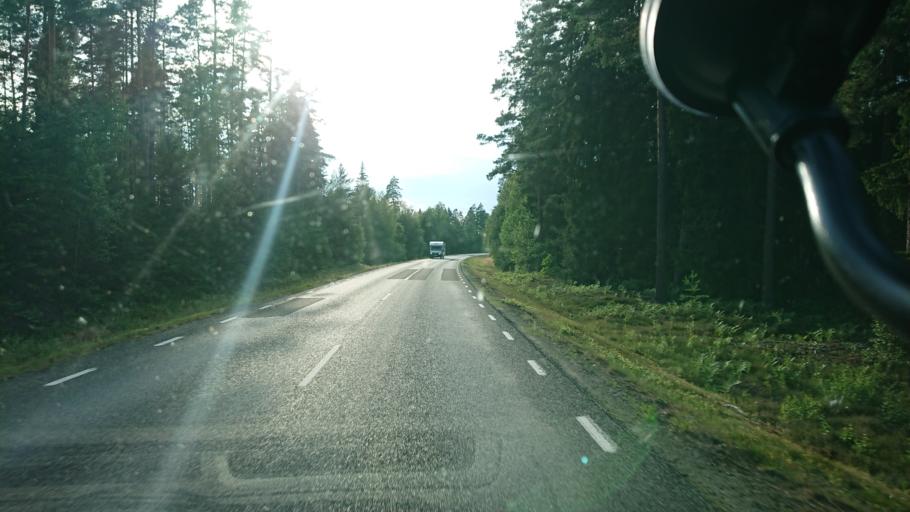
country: SE
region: Kronoberg
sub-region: Vaxjo Kommun
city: Braas
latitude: 57.0259
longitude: 14.9832
